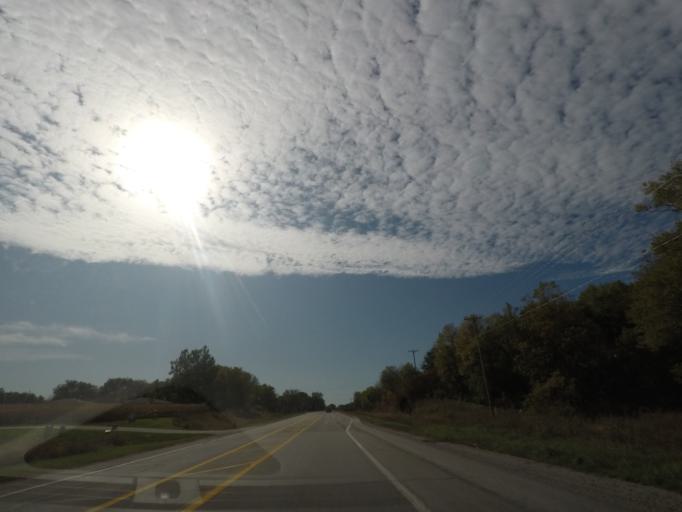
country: US
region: Iowa
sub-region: Story County
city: Gilbert
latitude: 42.0799
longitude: -93.6207
